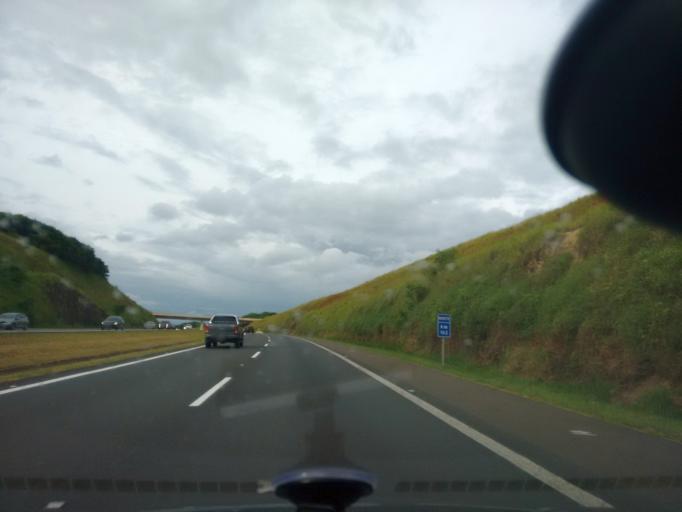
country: BR
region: Sao Paulo
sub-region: Cordeiropolis
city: Cordeiropolis
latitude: -22.5381
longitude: -47.4519
